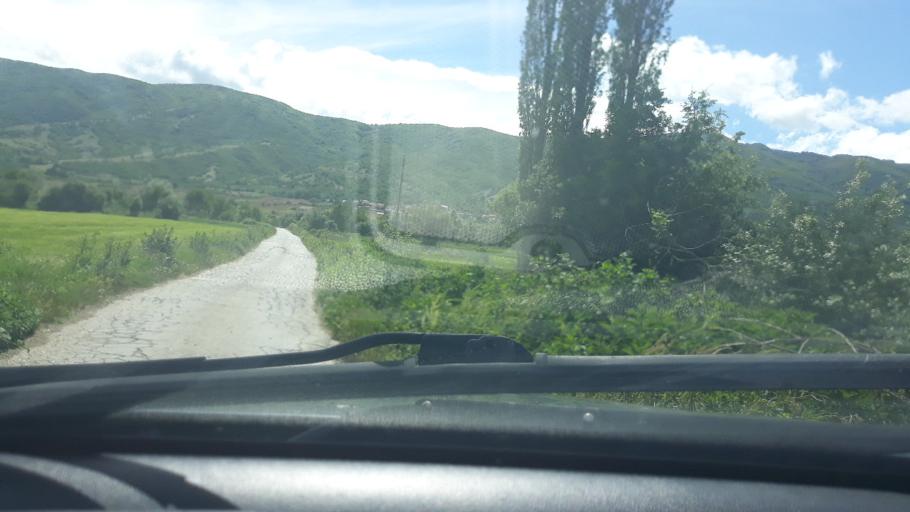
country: MK
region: Krivogastani
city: Krivogashtani
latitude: 41.3417
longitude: 21.3141
